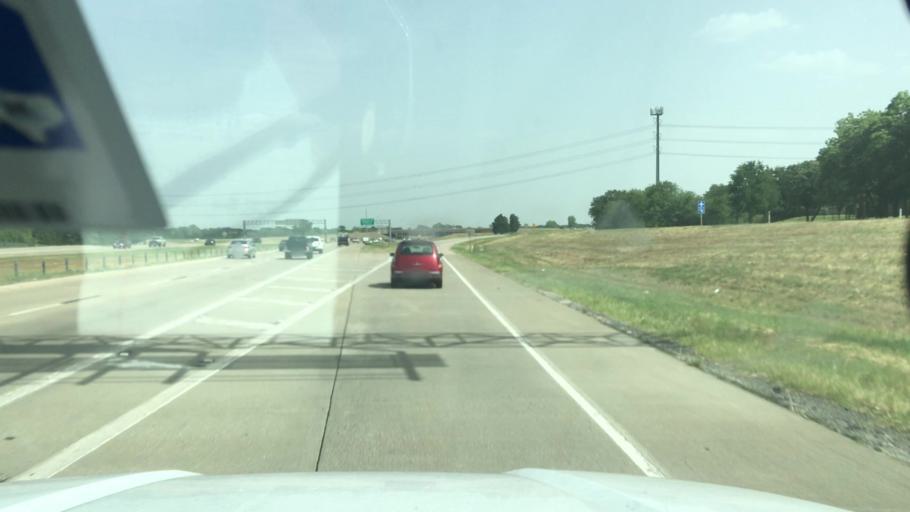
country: US
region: Texas
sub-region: Tarrant County
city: Euless
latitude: 32.8726
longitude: -97.0694
